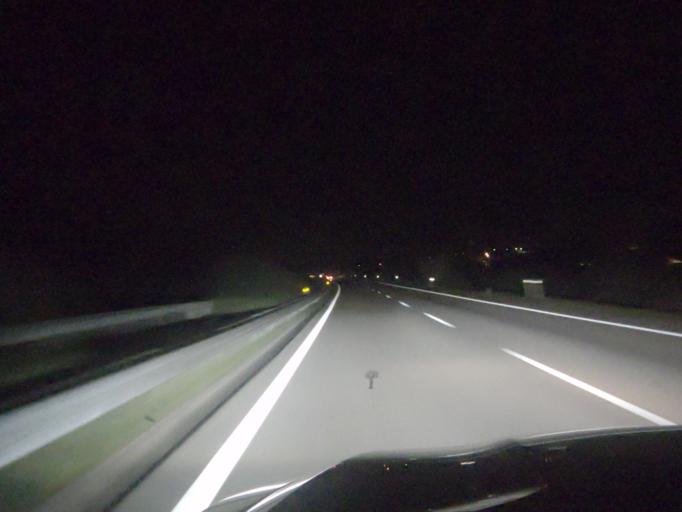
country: PT
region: Aveiro
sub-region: Mealhada
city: Mealhada
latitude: 40.4036
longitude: -8.4912
